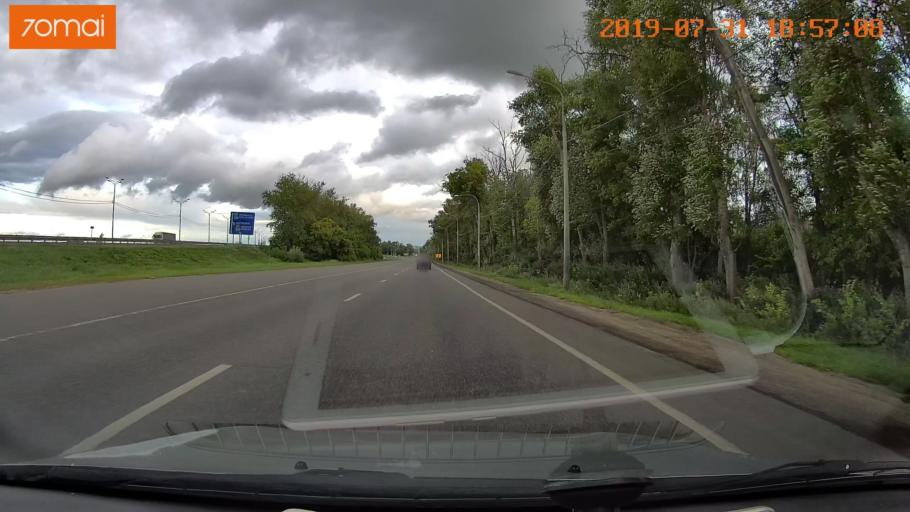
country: RU
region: Moskovskaya
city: Raduzhnyy
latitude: 55.1566
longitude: 38.6880
